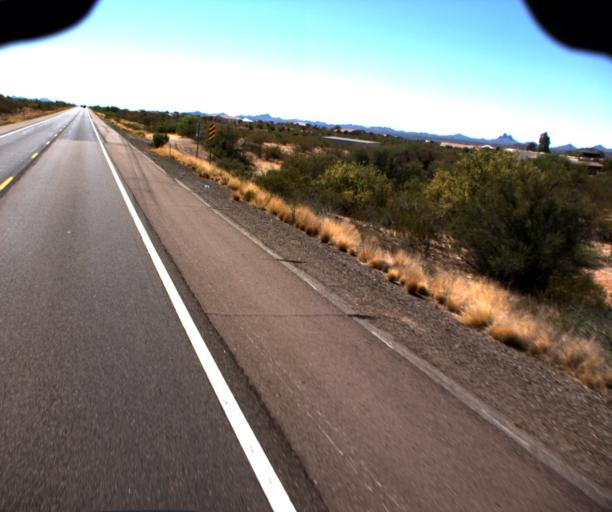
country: US
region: Arizona
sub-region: Yavapai County
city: Congress
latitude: 34.0449
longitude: -112.8379
